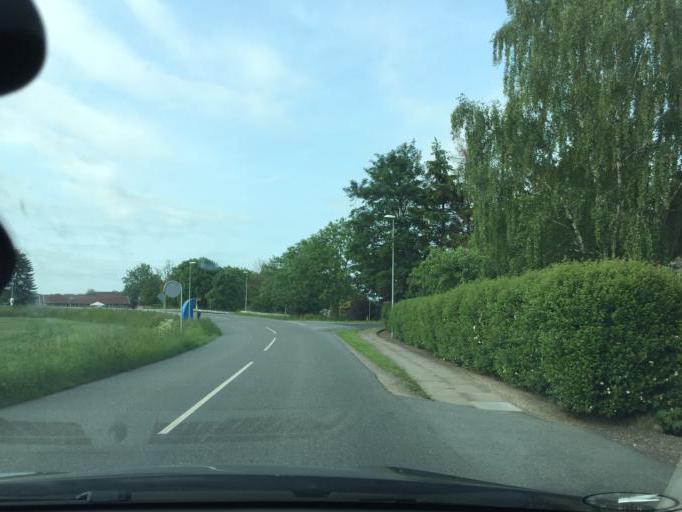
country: DK
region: South Denmark
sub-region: Odense Kommune
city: Bellinge
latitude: 55.3451
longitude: 10.3341
